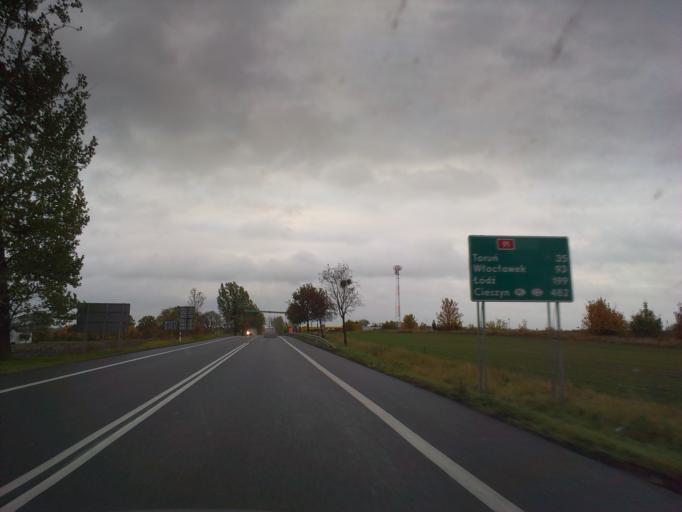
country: PL
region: Kujawsko-Pomorskie
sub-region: Powiat chelminski
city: Chelmno
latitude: 53.3185
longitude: 18.5055
